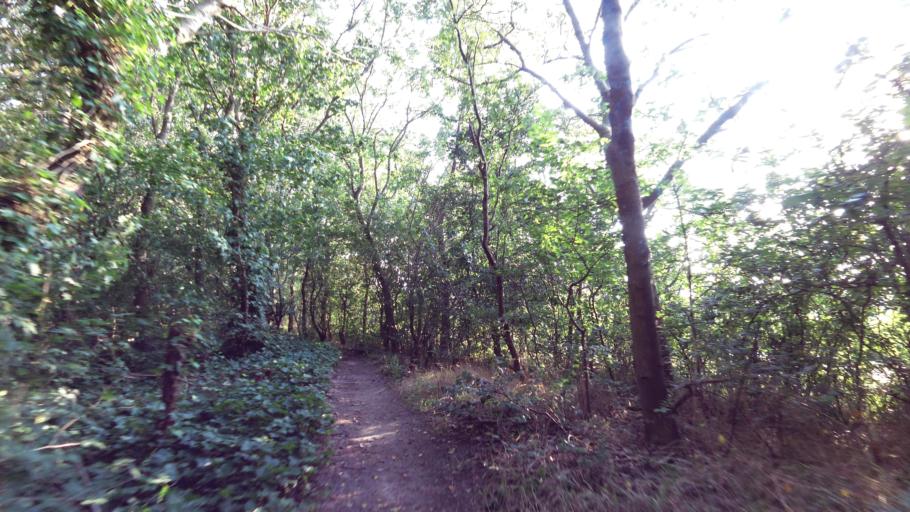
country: NL
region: South Holland
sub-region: Gemeente Noordwijkerhout
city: Noordwijkerhout
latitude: 52.2728
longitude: 4.4969
